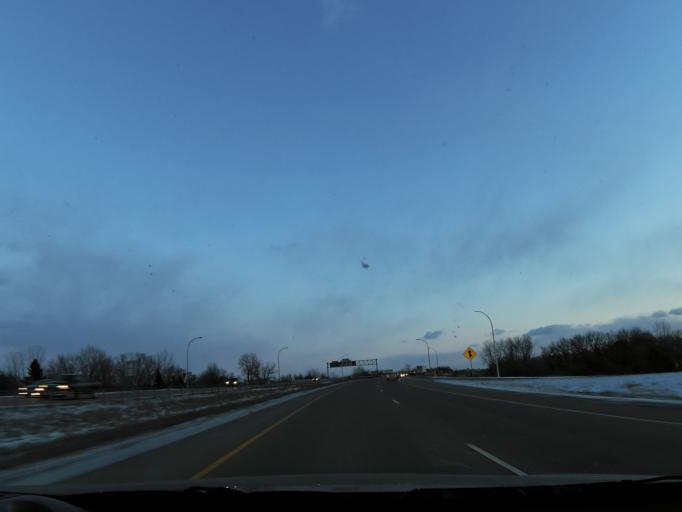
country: US
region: Minnesota
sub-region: Ramsey County
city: North Saint Paul
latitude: 45.0282
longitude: -92.9610
